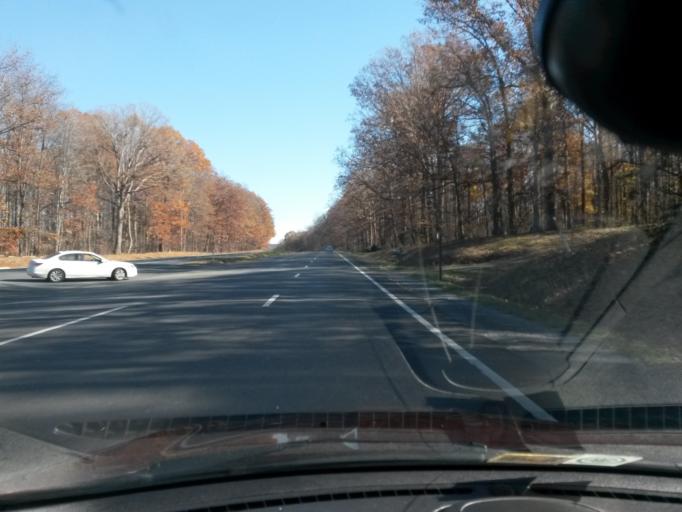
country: US
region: Virginia
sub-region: Bedford County
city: Forest
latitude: 37.3009
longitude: -79.3382
